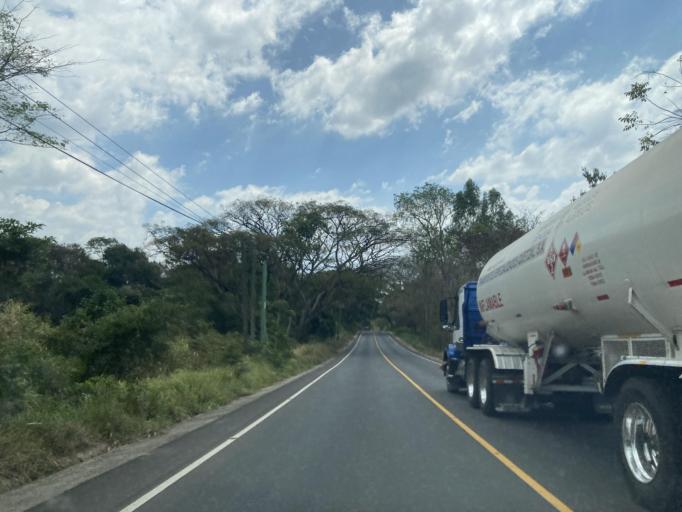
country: GT
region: Santa Rosa
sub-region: Municipio de Taxisco
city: Taxisco
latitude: 14.0806
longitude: -90.4876
